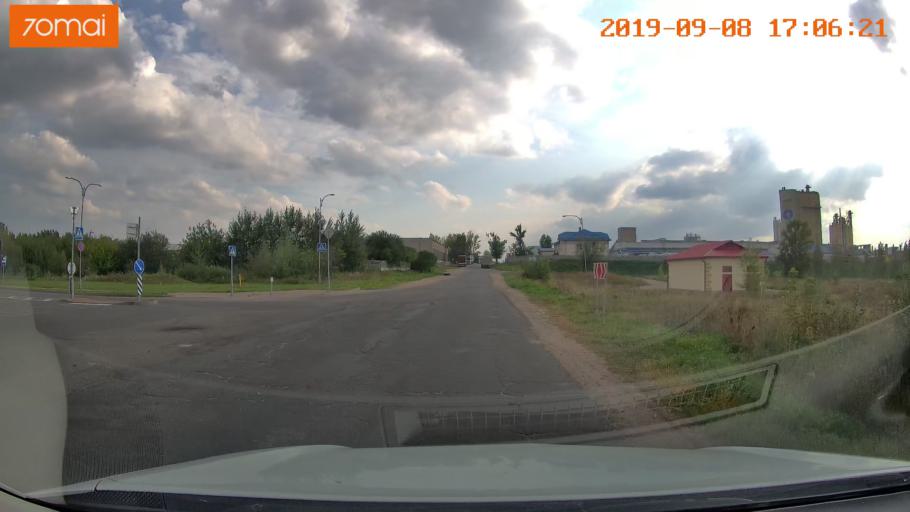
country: BY
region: Grodnenskaya
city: Hrodna
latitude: 53.6712
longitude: 23.9530
